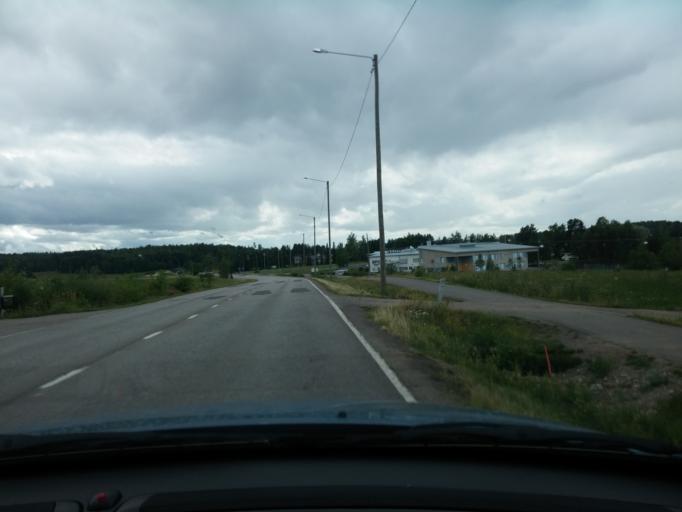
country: FI
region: Uusimaa
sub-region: Porvoo
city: Askola
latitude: 60.5262
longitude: 25.5903
